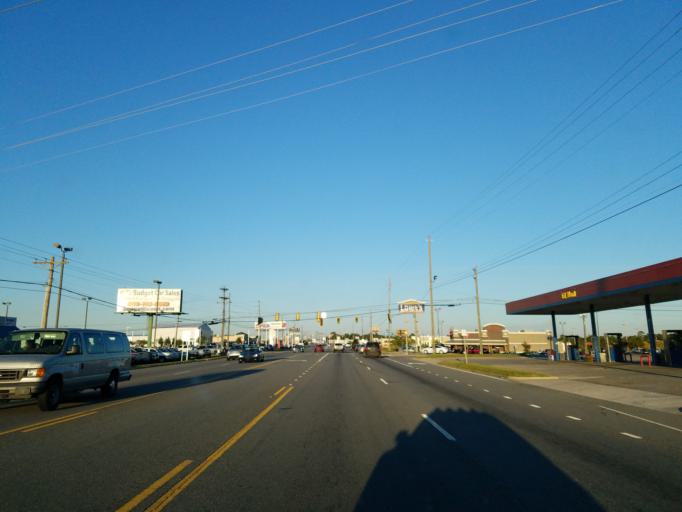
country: US
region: Georgia
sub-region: Tift County
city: Unionville
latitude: 31.4442
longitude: -83.5479
